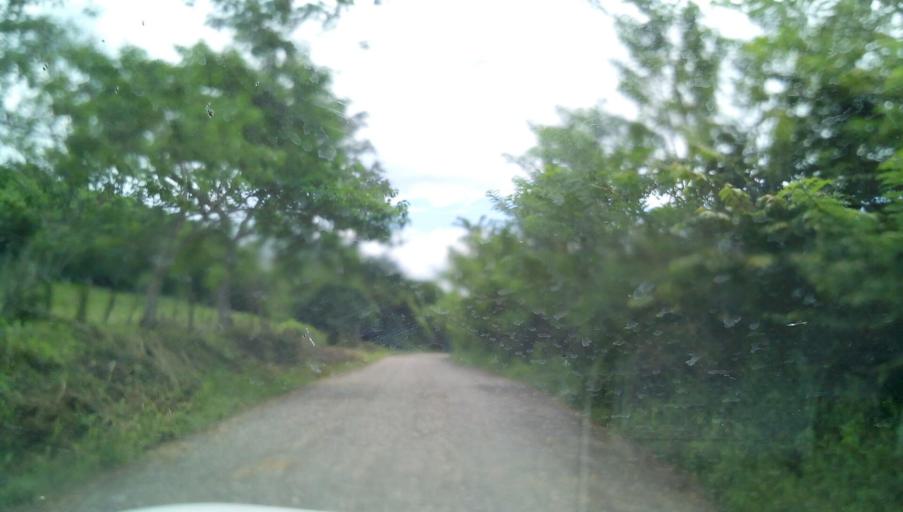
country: MX
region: Veracruz
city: Tepetzintla
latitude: 21.1422
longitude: -97.8531
